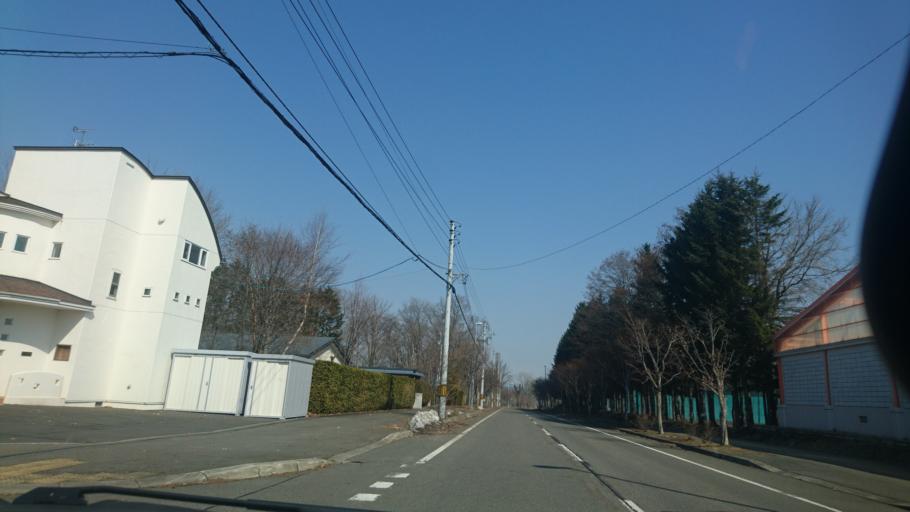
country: JP
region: Hokkaido
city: Obihiro
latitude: 42.9134
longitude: 143.0699
